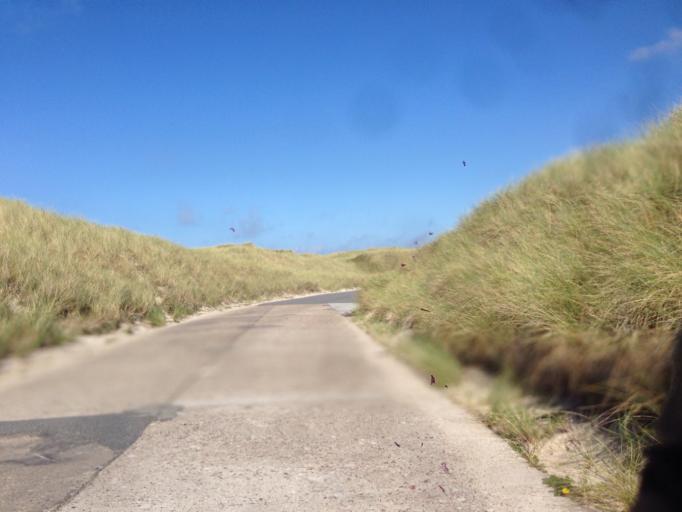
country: DE
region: Schleswig-Holstein
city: List
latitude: 55.0450
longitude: 8.3919
